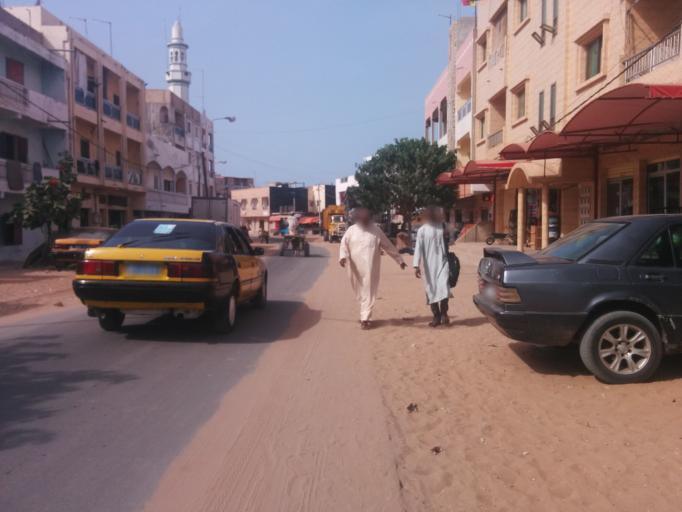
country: SN
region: Dakar
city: Pikine
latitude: 14.7635
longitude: -17.4374
